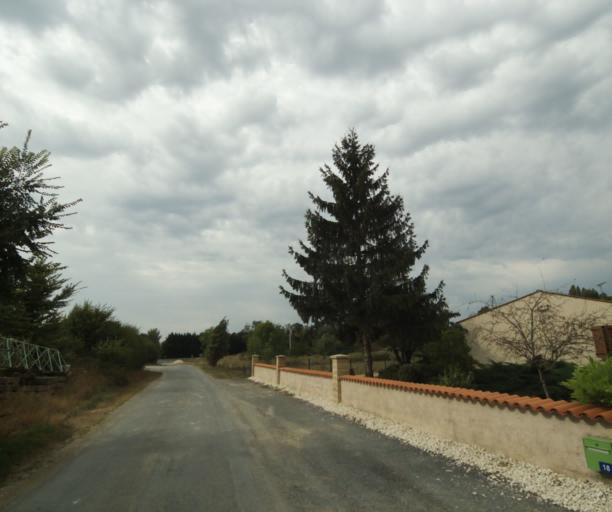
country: FR
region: Poitou-Charentes
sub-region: Departement de la Charente-Maritime
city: Tonnay-Charente
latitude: 45.9534
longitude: -0.8719
